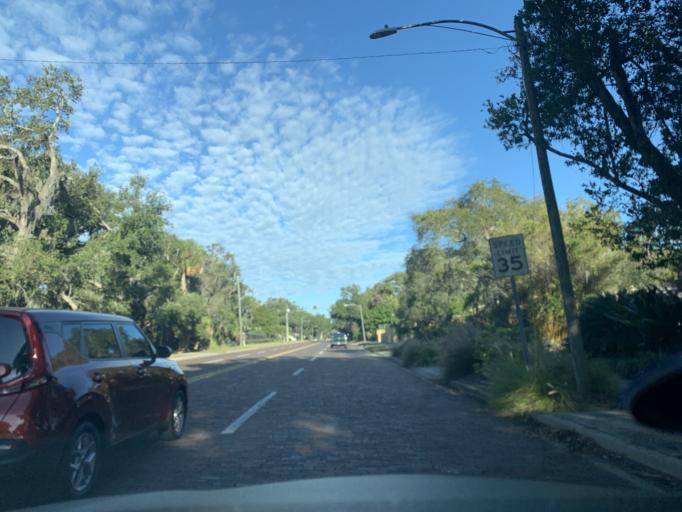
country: US
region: Florida
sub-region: Pinellas County
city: Treasure Island
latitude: 27.7853
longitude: -82.7502
